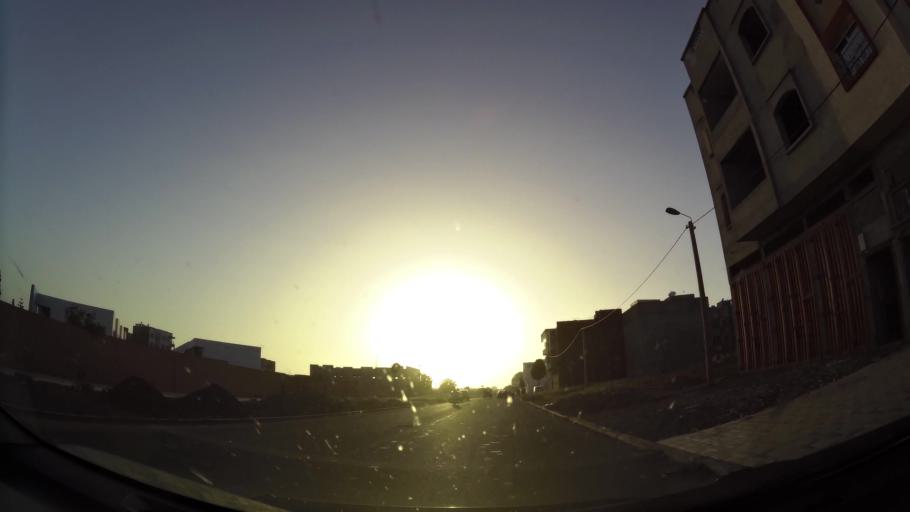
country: MA
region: Oued ed Dahab-Lagouira
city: Dakhla
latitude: 30.3958
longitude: -9.5632
